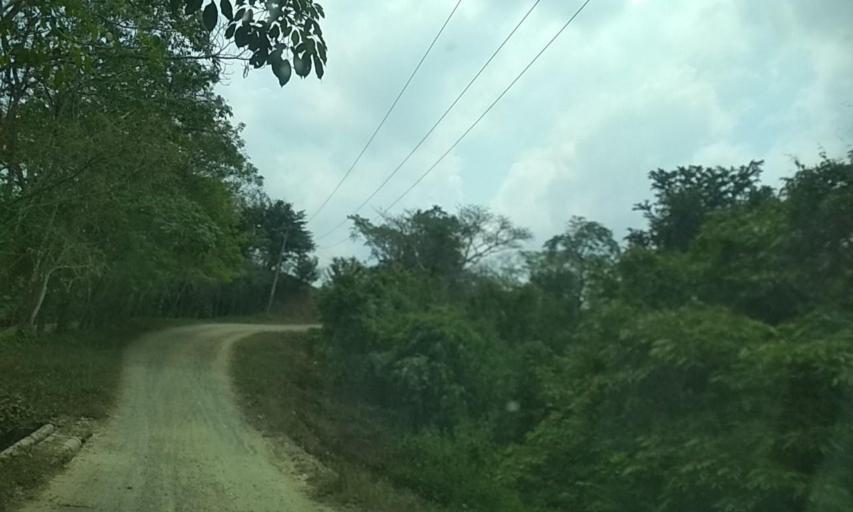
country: MX
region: Tabasco
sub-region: Huimanguillo
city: Francisco Rueda
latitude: 17.6016
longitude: -93.8033
